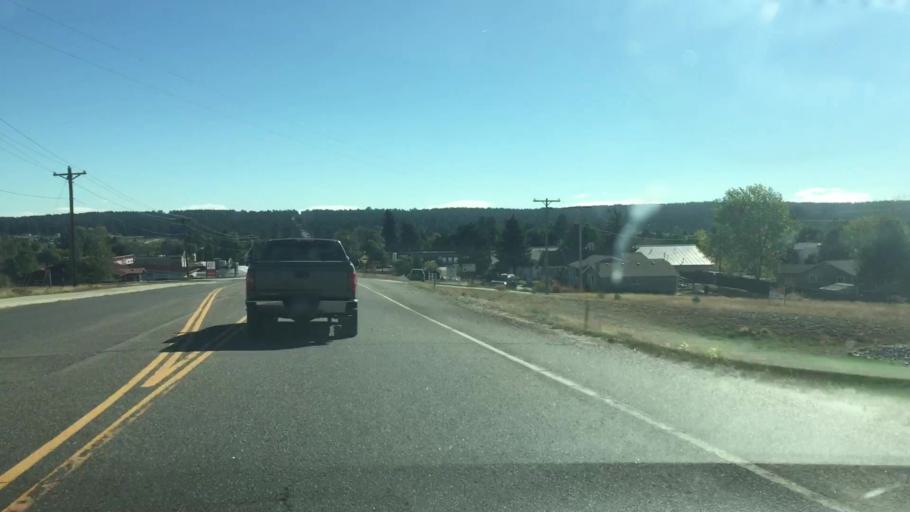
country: US
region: Colorado
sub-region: Elbert County
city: Elizabeth
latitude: 39.3615
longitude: -104.6042
